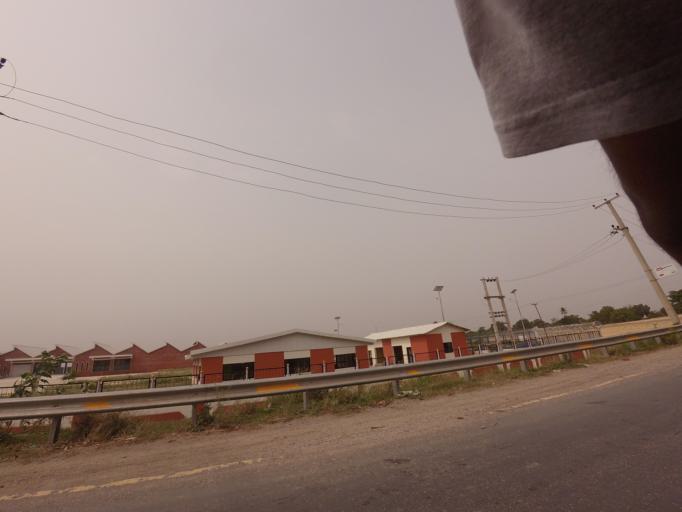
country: NP
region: Western Region
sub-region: Lumbini Zone
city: Bhairahawa
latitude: 27.5140
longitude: 83.3977
